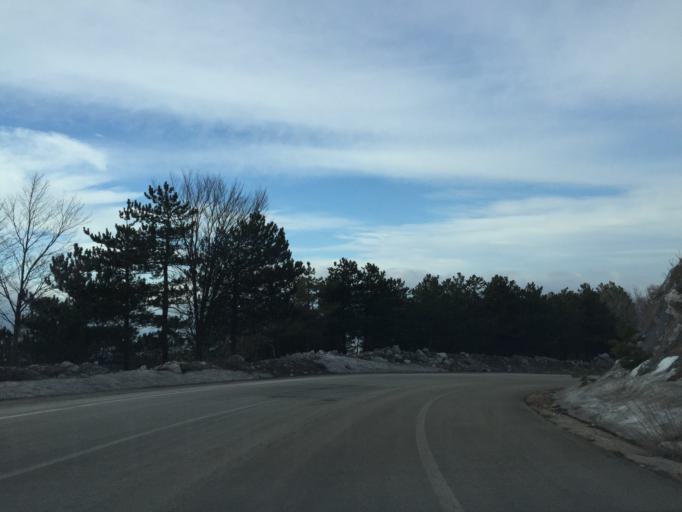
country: IT
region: Molise
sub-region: Provincia di Campobasso
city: San Massimo
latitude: 41.4694
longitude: 14.4131
